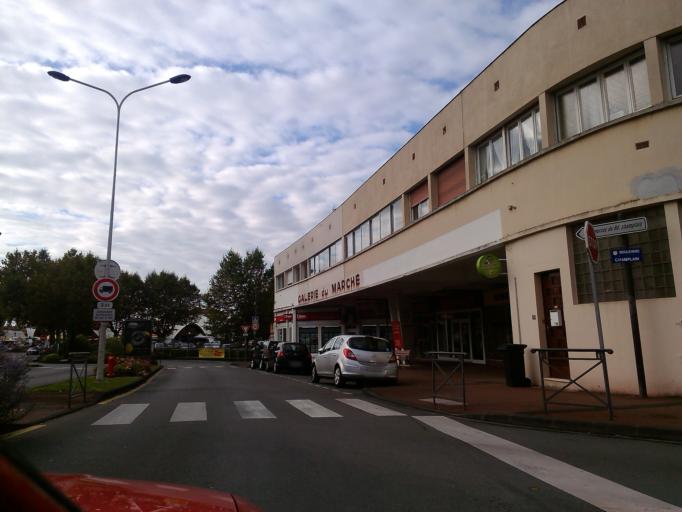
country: FR
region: Poitou-Charentes
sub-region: Departement de la Charente-Maritime
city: Royan
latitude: 45.6290
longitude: -1.0325
